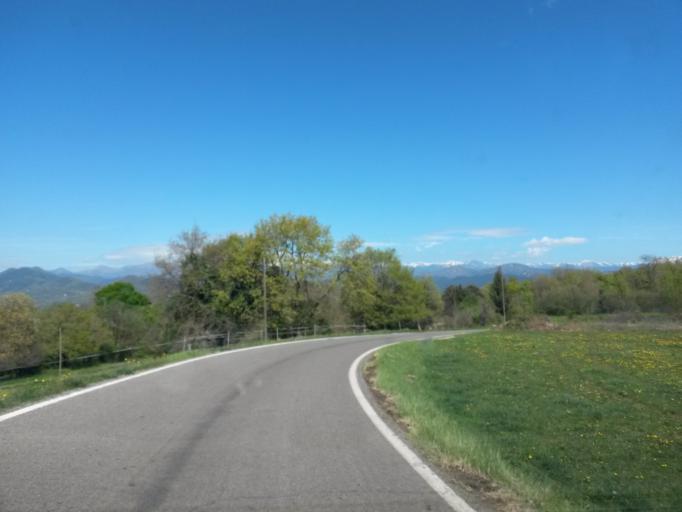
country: ES
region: Catalonia
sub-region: Provincia de Girona
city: Sant Cristofol de les Fonts
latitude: 42.1724
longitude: 2.5093
